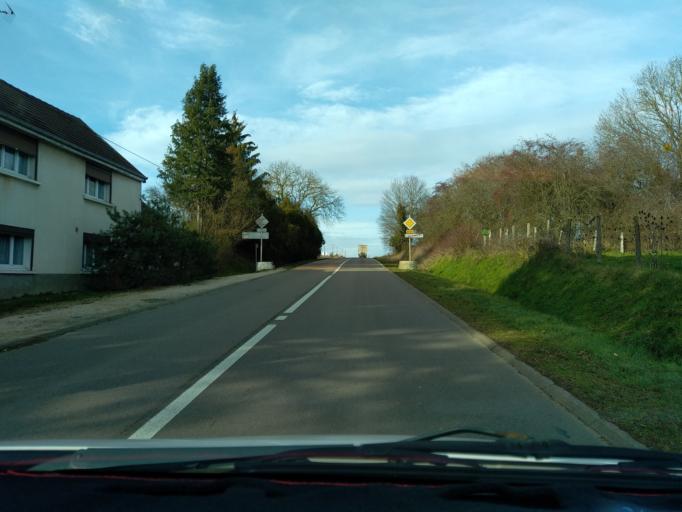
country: FR
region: Franche-Comte
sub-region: Departement de la Haute-Saone
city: Gray
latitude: 47.3931
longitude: 5.6513
